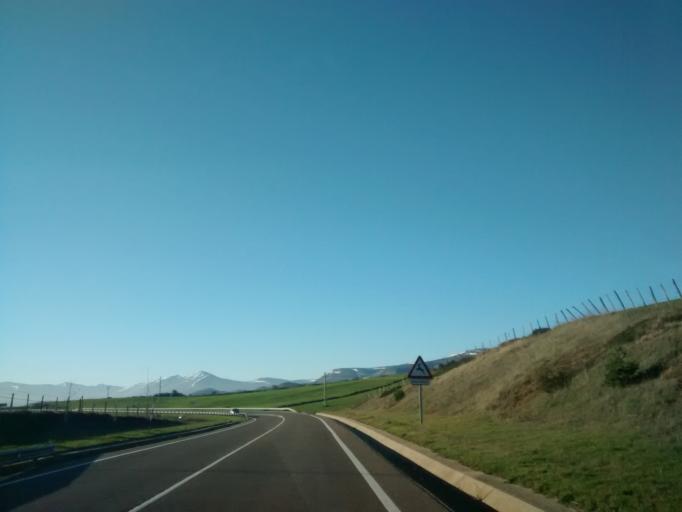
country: ES
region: Cantabria
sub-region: Provincia de Cantabria
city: Reinosa
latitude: 43.0055
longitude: -4.0924
